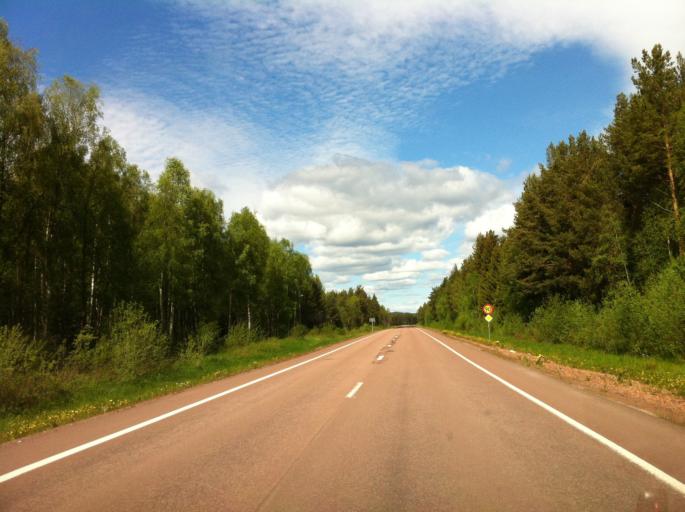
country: SE
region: Dalarna
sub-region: Mora Kommun
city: Mora
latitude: 60.9217
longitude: 14.5854
